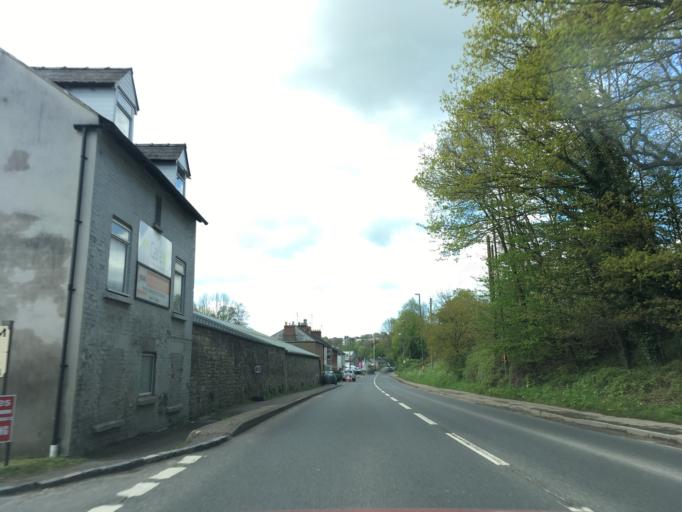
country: GB
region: England
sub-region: Gloucestershire
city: Stroud
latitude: 51.7301
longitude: -2.2038
